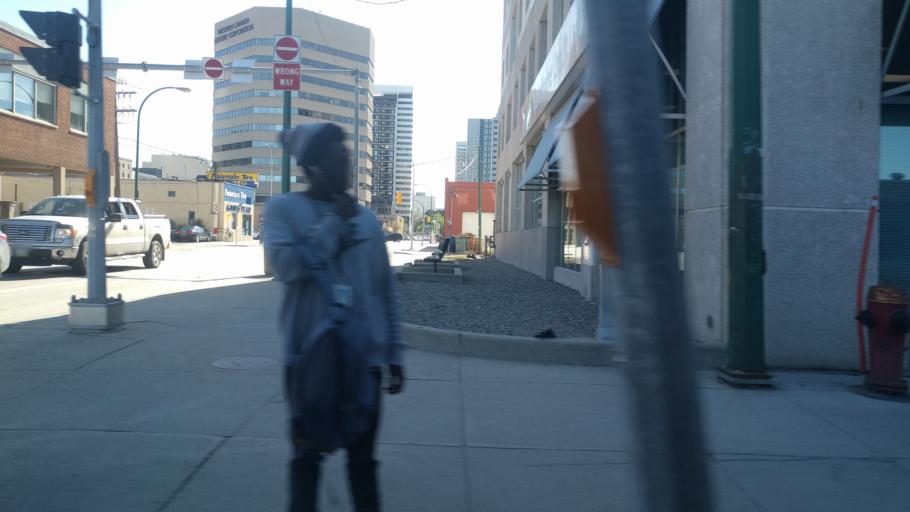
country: CA
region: Manitoba
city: Winnipeg
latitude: 49.8906
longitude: -97.1359
